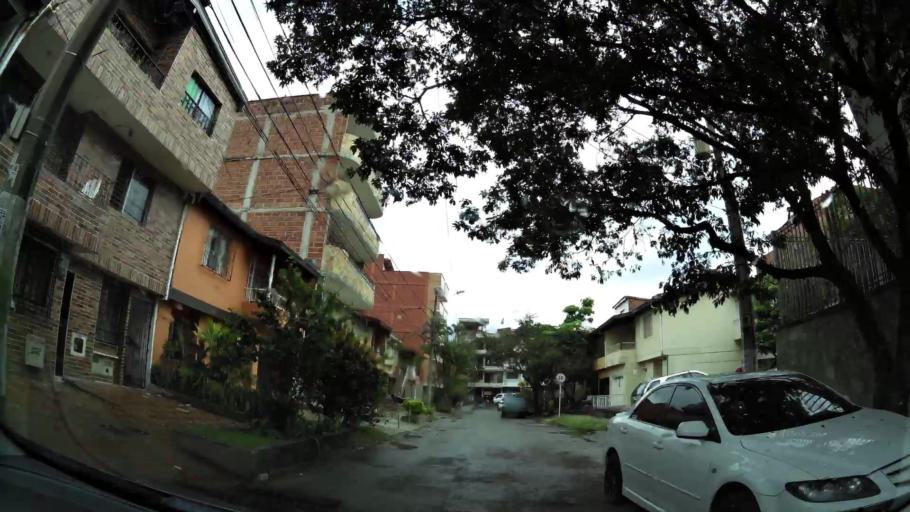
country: CO
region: Antioquia
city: Itagui
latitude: 6.1848
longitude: -75.5979
